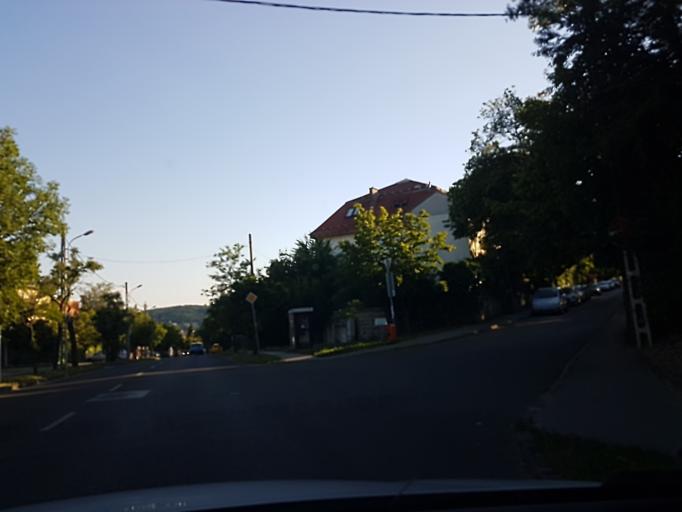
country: HU
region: Budapest
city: Budapest II. keruelet
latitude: 47.5194
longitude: 19.0218
